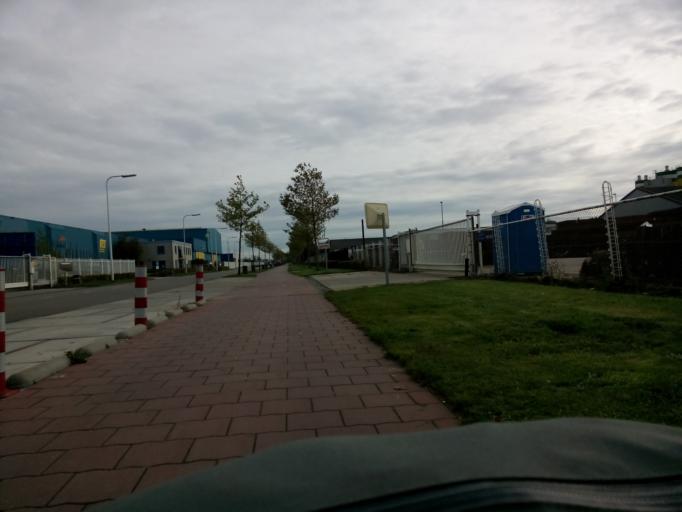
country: NL
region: Drenthe
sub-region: Gemeente Hoogeveen
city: Hoogeveen
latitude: 52.7301
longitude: 6.4948
